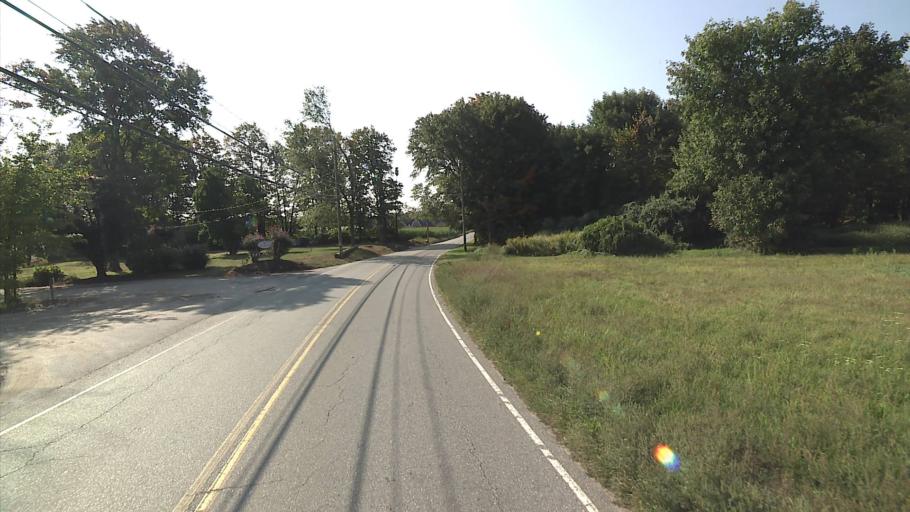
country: US
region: Connecticut
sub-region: Windham County
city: South Windham
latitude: 41.6255
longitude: -72.1977
